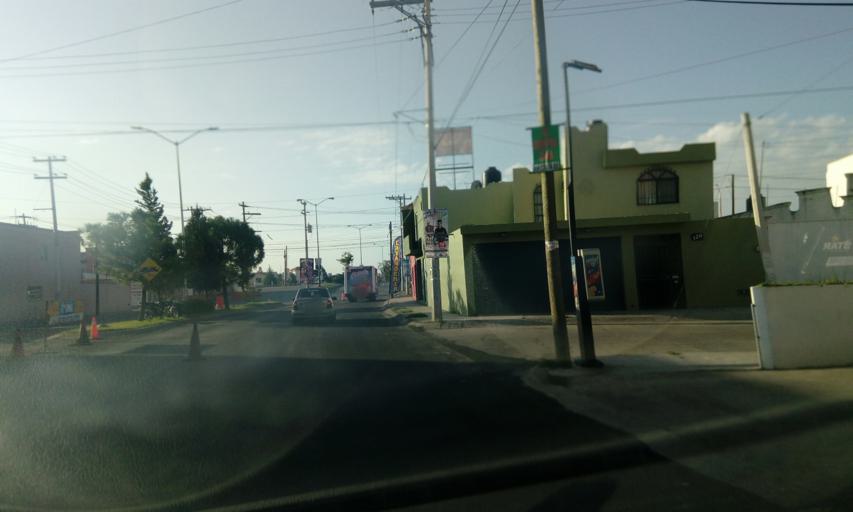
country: MX
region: Durango
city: Victoria de Durango
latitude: 24.0007
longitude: -104.6409
